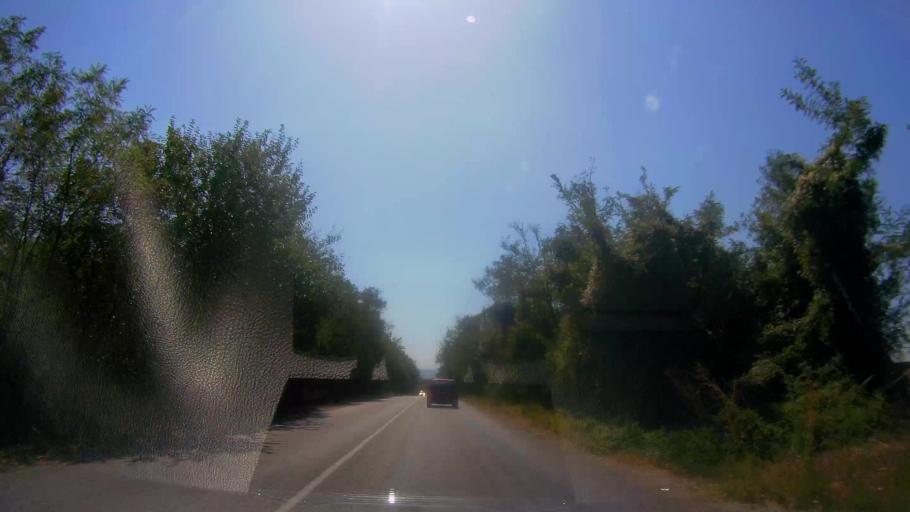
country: BG
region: Veliko Turnovo
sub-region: Obshtina Gorna Oryakhovitsa
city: Purvomaytsi
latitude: 43.2541
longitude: 25.6429
